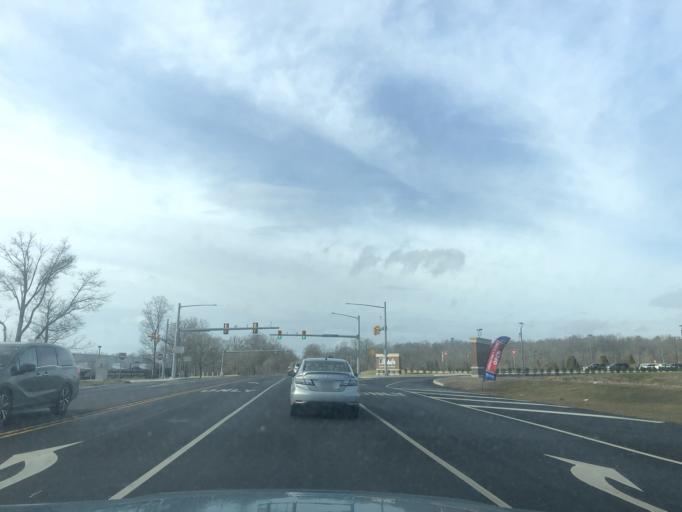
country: US
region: Pennsylvania
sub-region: Bucks County
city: Quakertown
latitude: 40.4432
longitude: -75.3743
